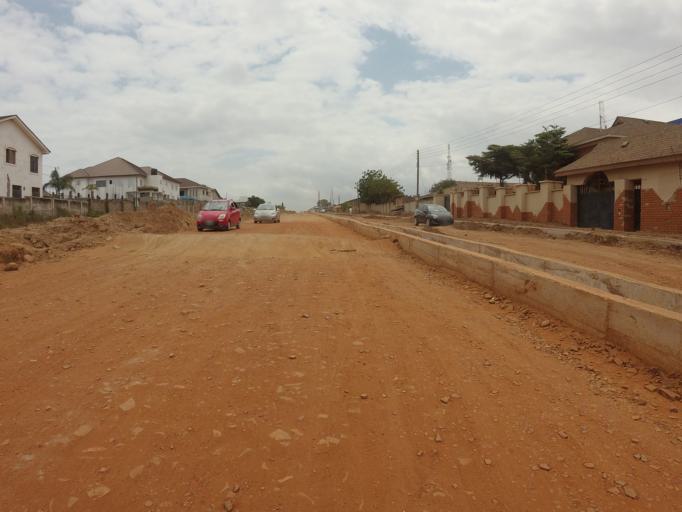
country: GH
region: Greater Accra
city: Medina Estates
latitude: 5.6295
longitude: -0.1421
